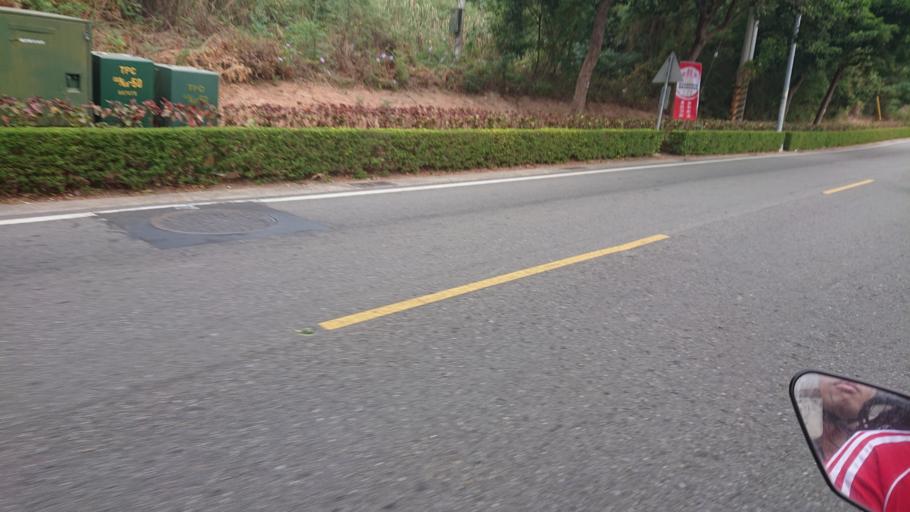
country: TW
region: Fukien
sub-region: Kinmen
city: Jincheng
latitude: 24.4181
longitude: 118.3097
